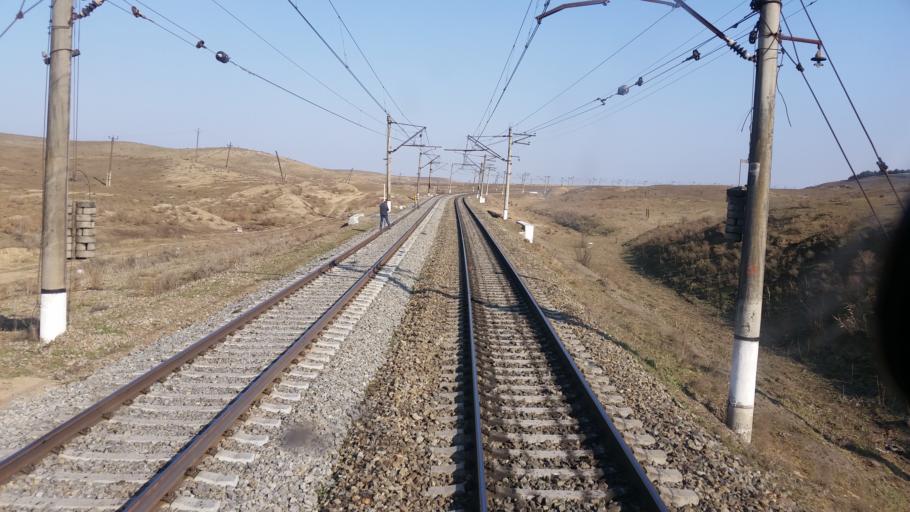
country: AZ
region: Haciqabul
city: Haciqabul
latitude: 40.0479
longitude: 48.9769
